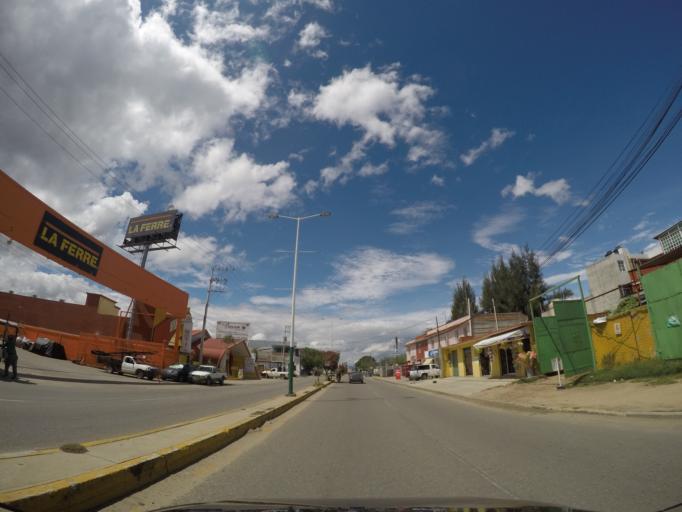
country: MX
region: Oaxaca
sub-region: Santa Cruz Xoxocotlan
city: Santa Cruz Xoxocotlan
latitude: 17.0219
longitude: -96.7305
